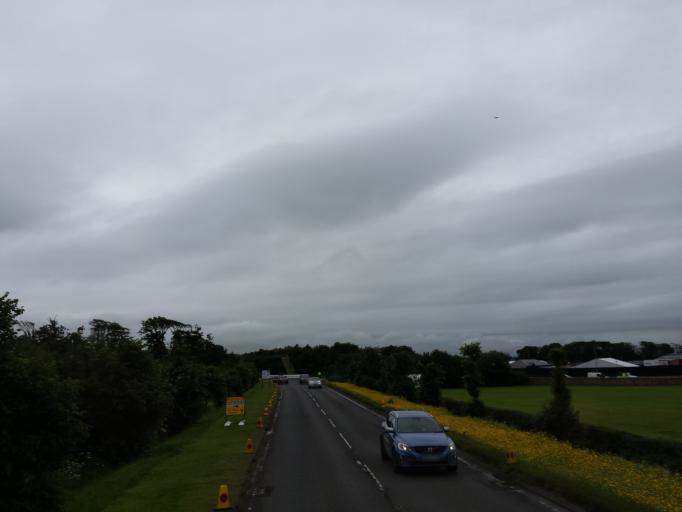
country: GB
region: Scotland
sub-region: Fife
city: Saint Andrews
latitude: 56.3446
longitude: -2.8179
